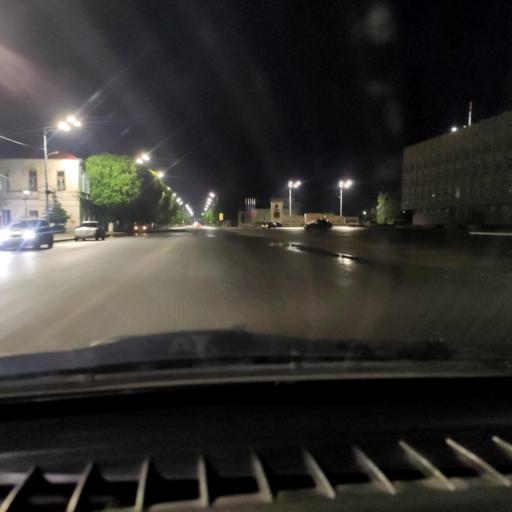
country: RU
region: Samara
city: Syzran'
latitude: 53.1555
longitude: 48.4741
